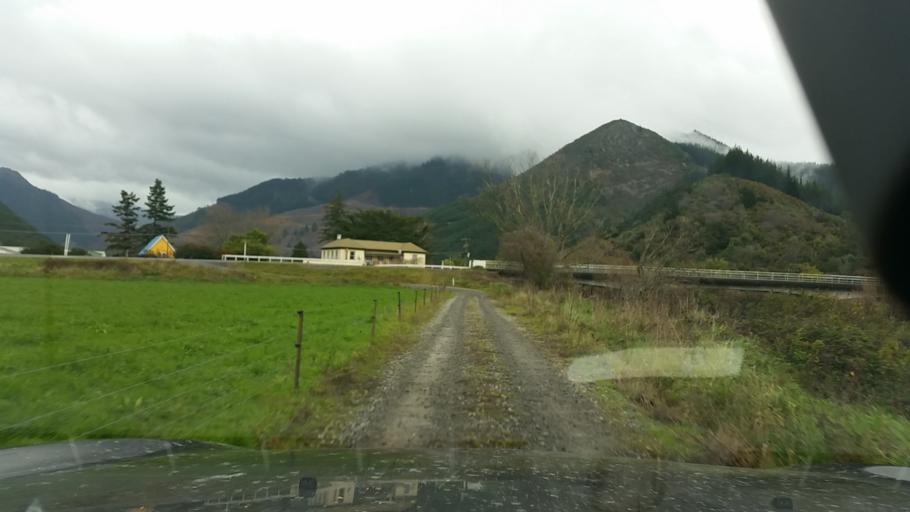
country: NZ
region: Marlborough
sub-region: Marlborough District
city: Picton
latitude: -41.2897
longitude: 173.6709
